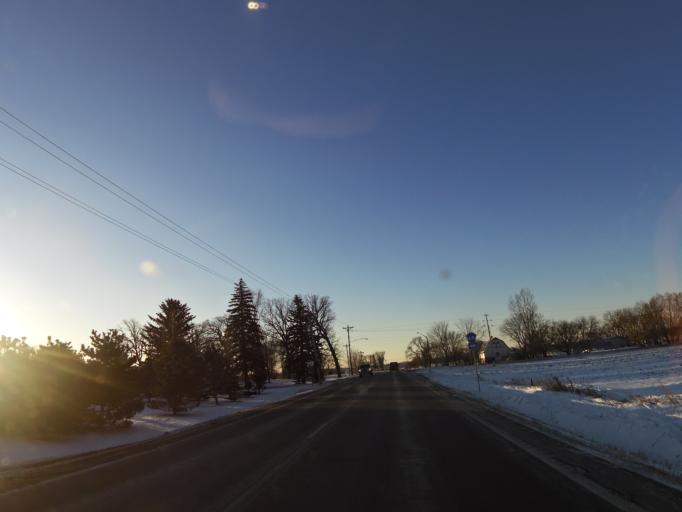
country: US
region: Minnesota
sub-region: Scott County
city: Prior Lake
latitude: 44.6754
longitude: -93.3792
